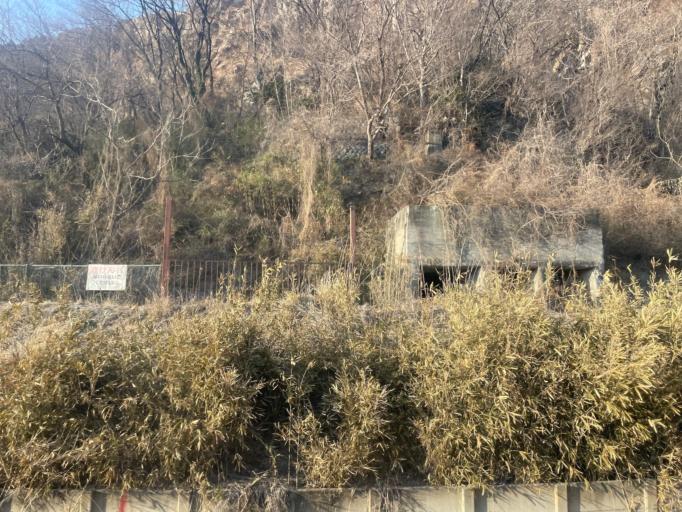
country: JP
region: Gunma
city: Nakanojomachi
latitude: 36.5526
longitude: 138.9234
